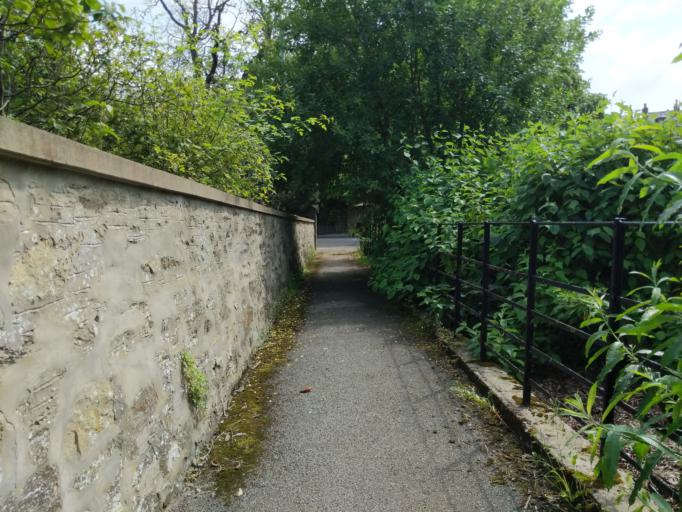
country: GB
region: Scotland
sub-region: Moray
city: Keith
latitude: 57.5437
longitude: -2.9532
